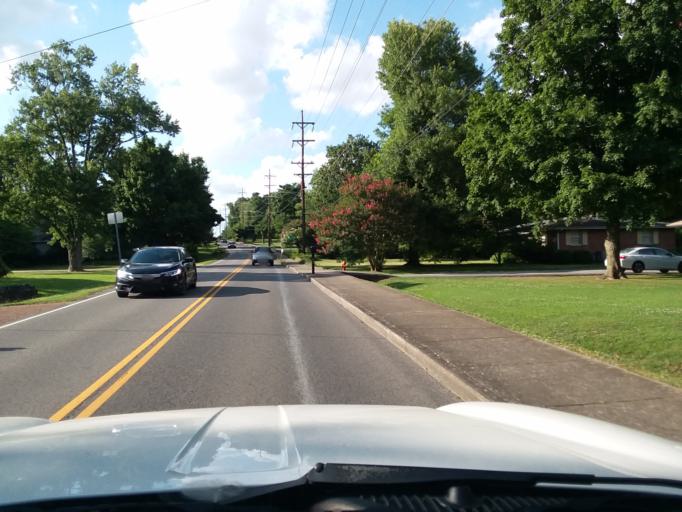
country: US
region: Tennessee
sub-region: Davidson County
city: Oak Hill
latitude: 36.0705
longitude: -86.7587
